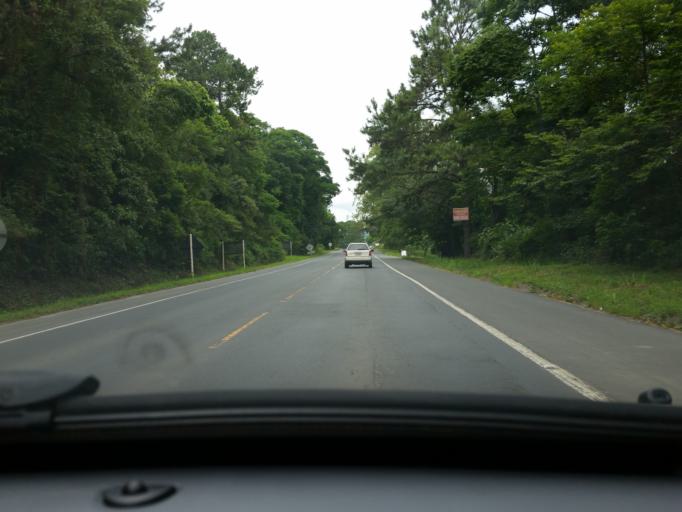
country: BR
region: Santa Catarina
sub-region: Rio Do Sul
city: Rio do Sul
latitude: -27.2561
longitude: -49.7097
